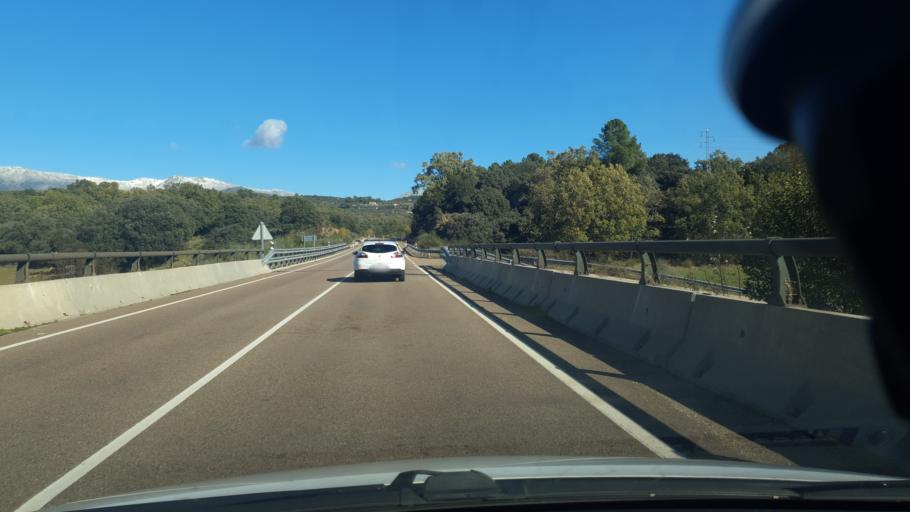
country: ES
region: Castille and Leon
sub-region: Provincia de Avila
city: Arenas de San Pedro
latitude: 40.1814
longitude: -5.0863
